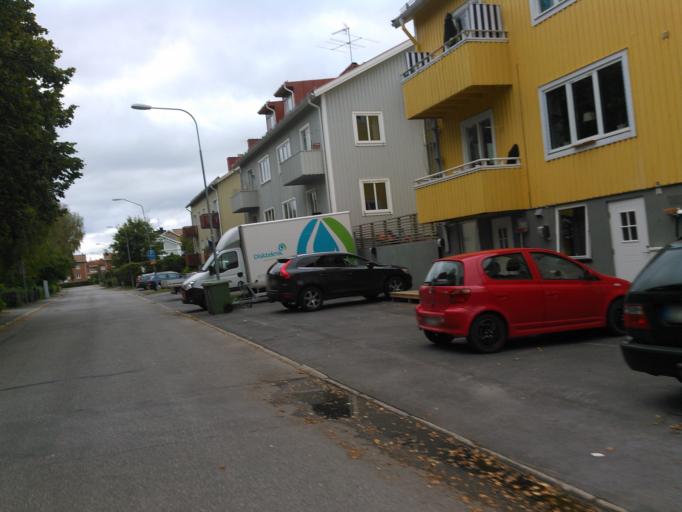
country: SE
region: Vaesterbotten
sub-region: Umea Kommun
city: Umea
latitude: 63.8181
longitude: 20.2886
